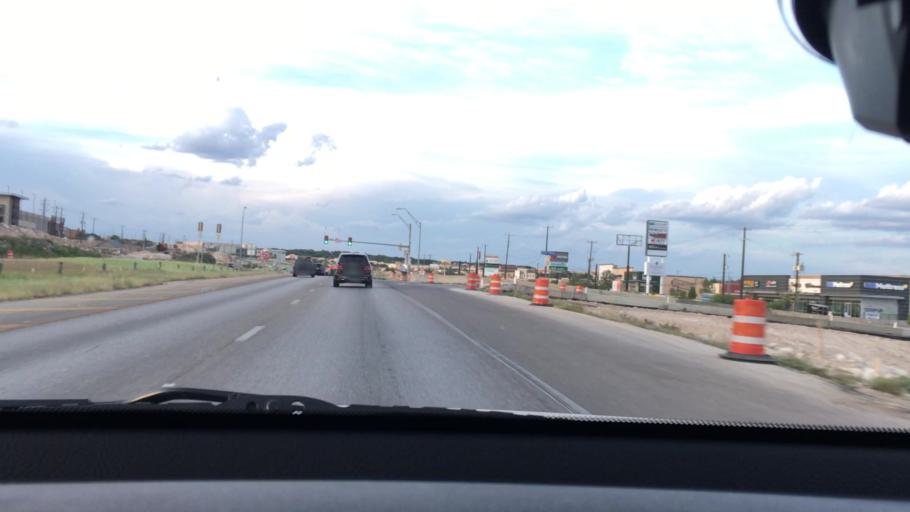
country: US
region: Texas
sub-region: Bexar County
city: Hollywood Park
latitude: 29.6443
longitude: -98.4524
